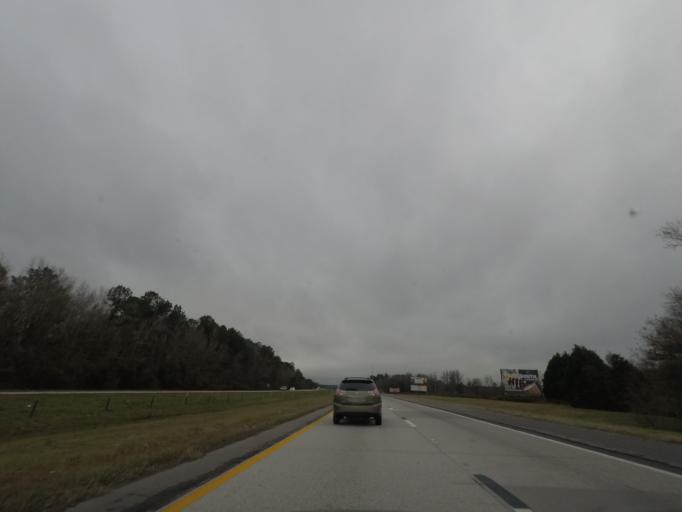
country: US
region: South Carolina
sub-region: Dorchester County
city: Saint George
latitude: 33.2199
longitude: -80.5970
